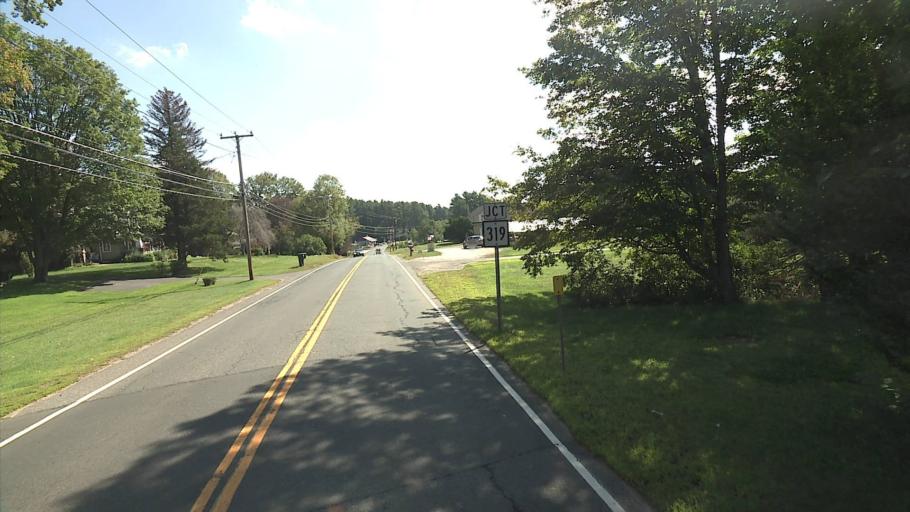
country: US
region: Connecticut
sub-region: Tolland County
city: Stafford Springs
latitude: 41.9707
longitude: -72.3391
